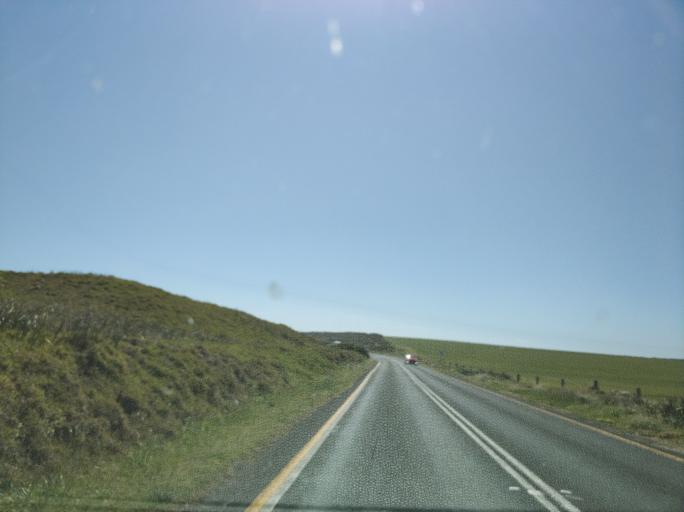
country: AU
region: Victoria
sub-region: Colac-Otway
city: Apollo Bay
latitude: -38.6693
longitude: 143.1141
